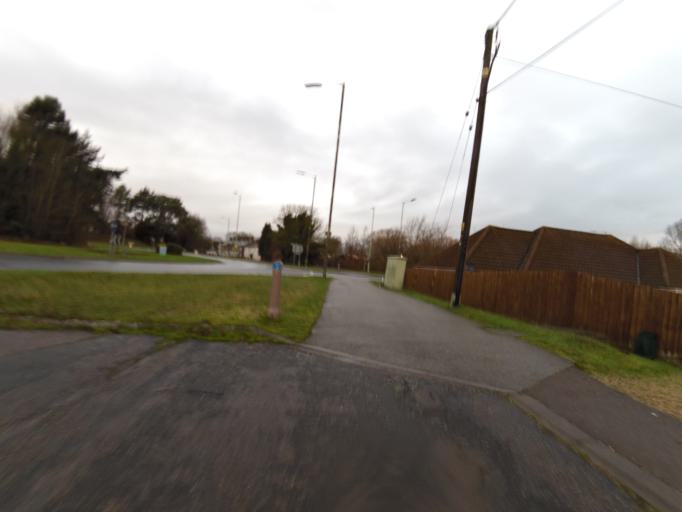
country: GB
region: England
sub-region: Suffolk
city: Stowmarket
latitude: 52.1798
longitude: 1.0061
